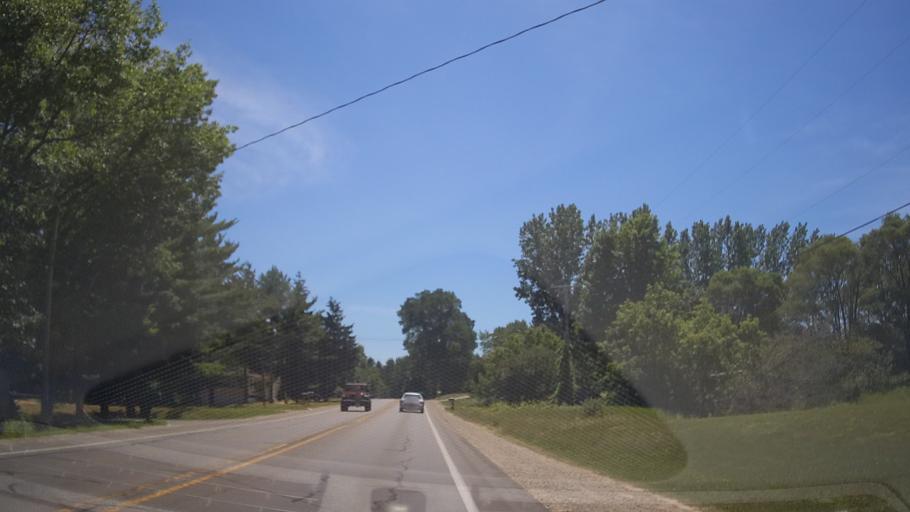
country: US
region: Michigan
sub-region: Grand Traverse County
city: Traverse City
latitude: 44.7087
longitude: -85.6923
